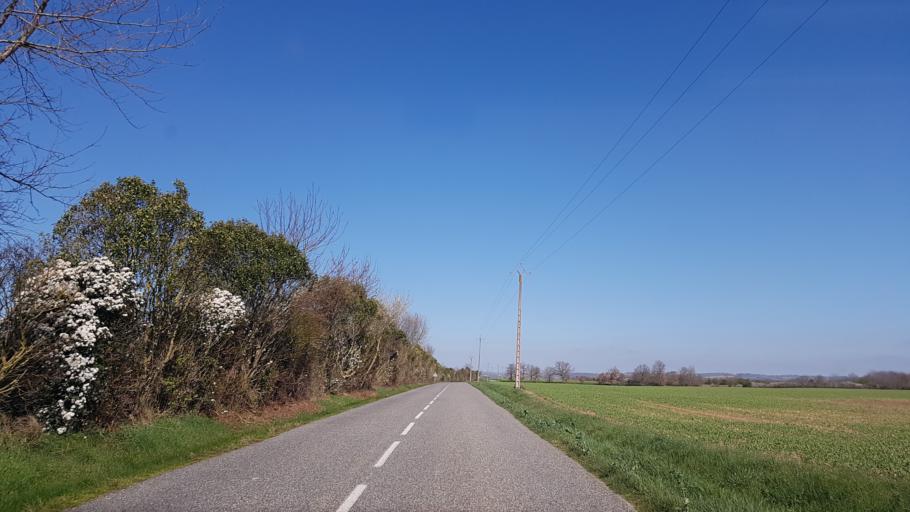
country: FR
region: Languedoc-Roussillon
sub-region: Departement de l'Aude
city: Belpech
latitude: 43.1597
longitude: 1.7090
